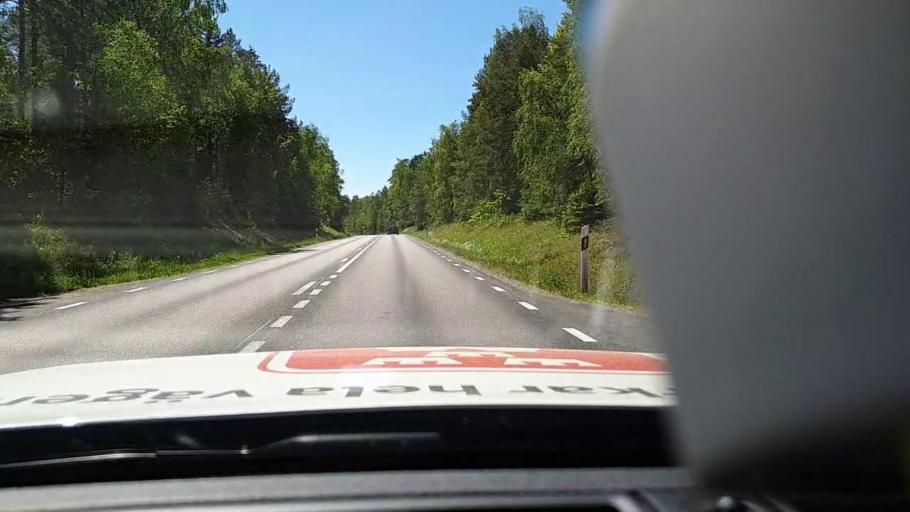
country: SE
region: Uppsala
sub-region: Uppsala Kommun
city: Saevja
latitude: 59.7925
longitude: 17.6742
